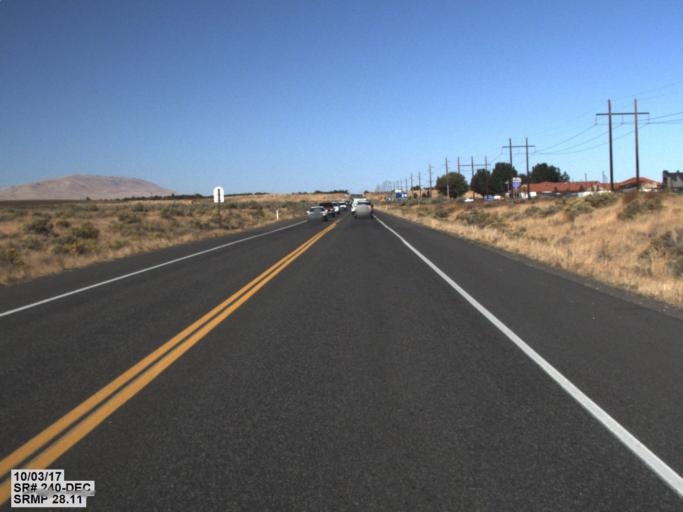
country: US
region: Washington
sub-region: Benton County
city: Richland
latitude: 46.3156
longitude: -119.2965
